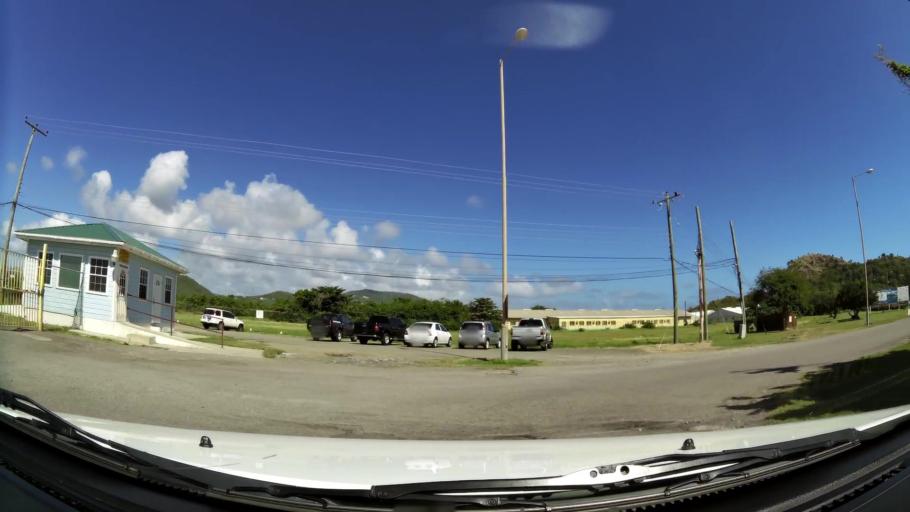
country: LC
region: Vieux-Fort
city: Vieux Fort
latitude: 13.7374
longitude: -60.9510
